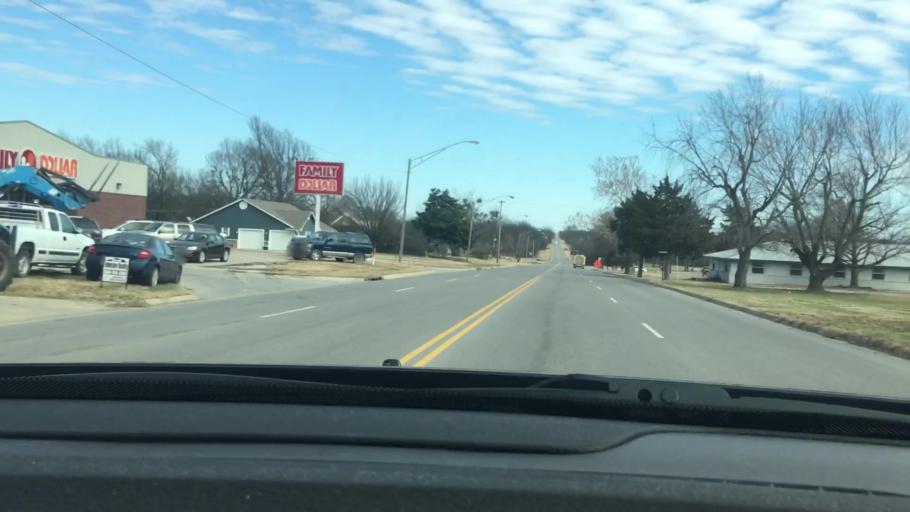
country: US
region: Oklahoma
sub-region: Garvin County
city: Stratford
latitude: 34.7966
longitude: -96.9520
